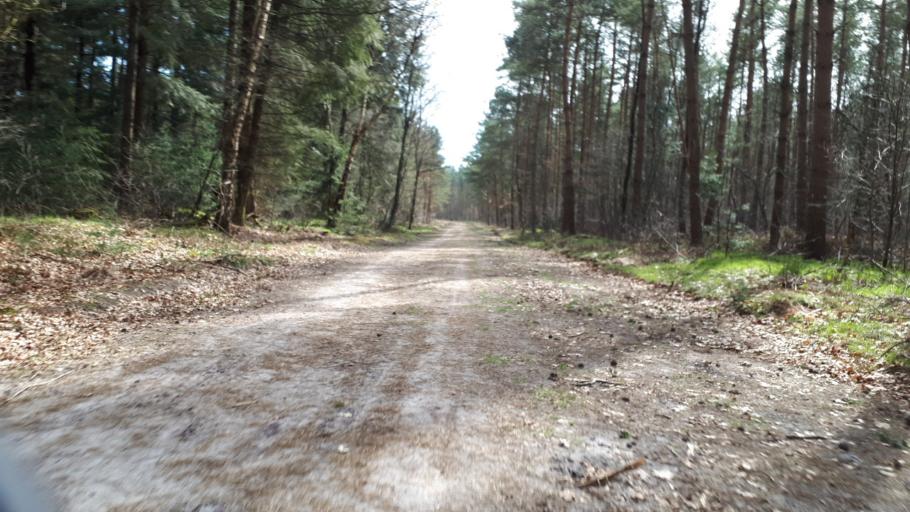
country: DE
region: Lower Saxony
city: Grossenkneten
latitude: 53.0362
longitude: 8.2825
